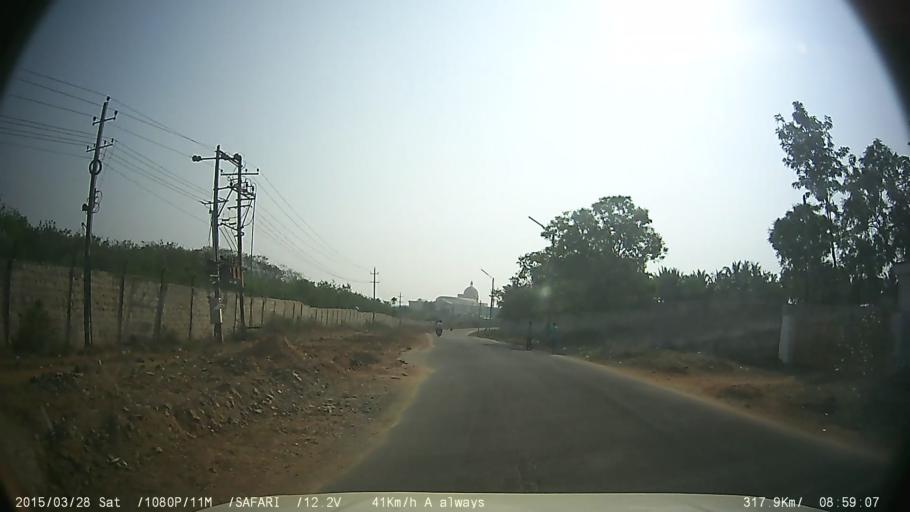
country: IN
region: Karnataka
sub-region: Mysore
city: Mysore
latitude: 12.3567
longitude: 76.5871
